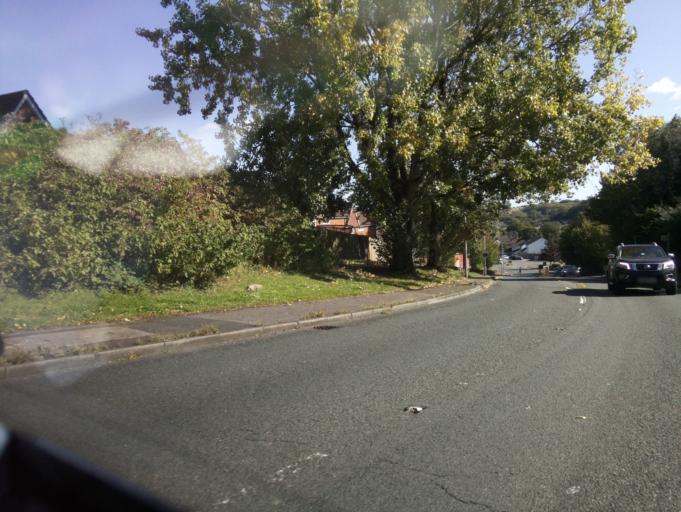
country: GB
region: Wales
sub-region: Newport
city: Caerleon
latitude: 51.5979
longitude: -2.9393
